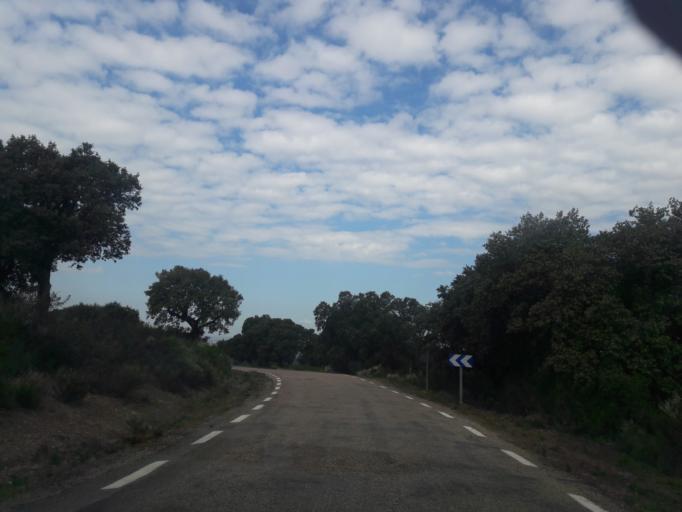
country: ES
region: Castille and Leon
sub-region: Provincia de Salamanca
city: Serradilla del Arroyo
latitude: 40.5418
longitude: -6.4027
